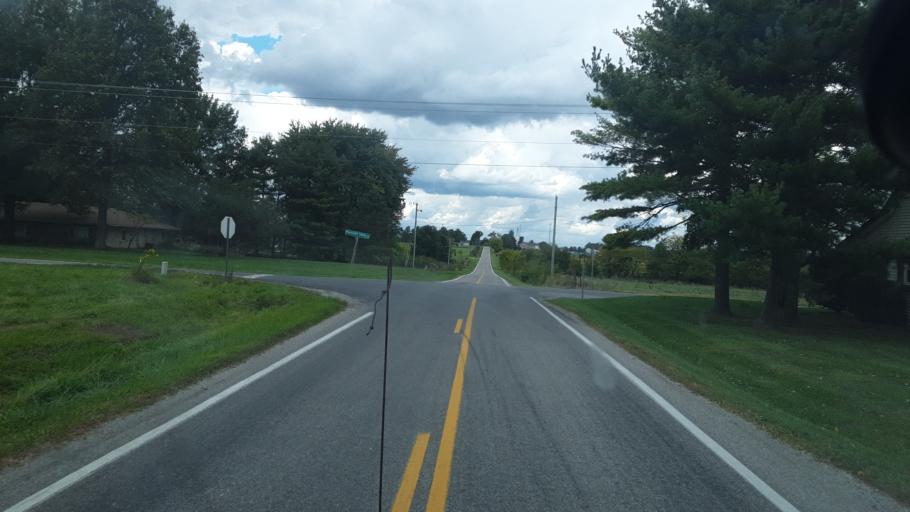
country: US
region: Ohio
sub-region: Knox County
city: Centerburg
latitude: 40.2606
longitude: -82.7520
